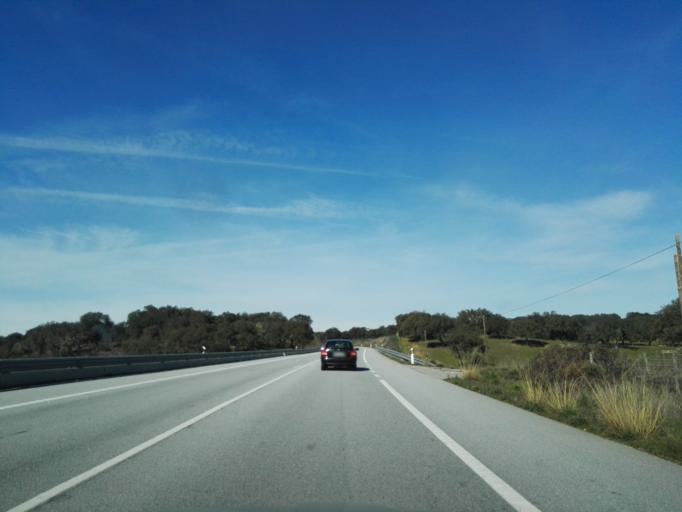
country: PT
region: Portalegre
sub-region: Portalegre
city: Alegrete
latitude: 39.1826
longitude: -7.3450
